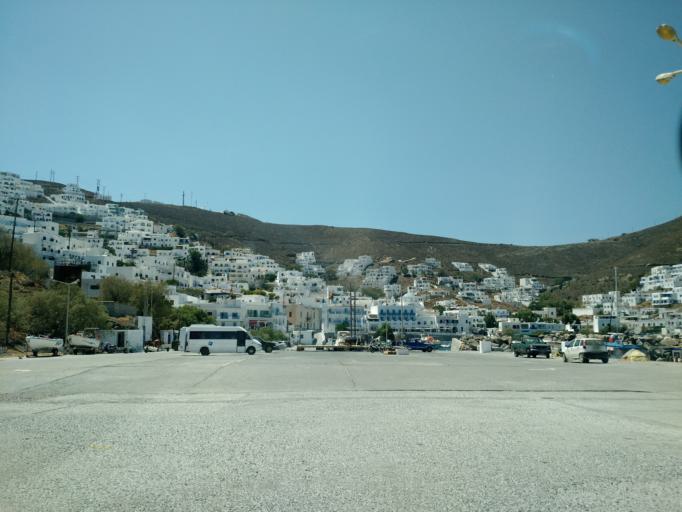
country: GR
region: South Aegean
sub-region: Nomos Dodekanisou
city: Astypalaia
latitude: 36.5470
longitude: 26.3556
